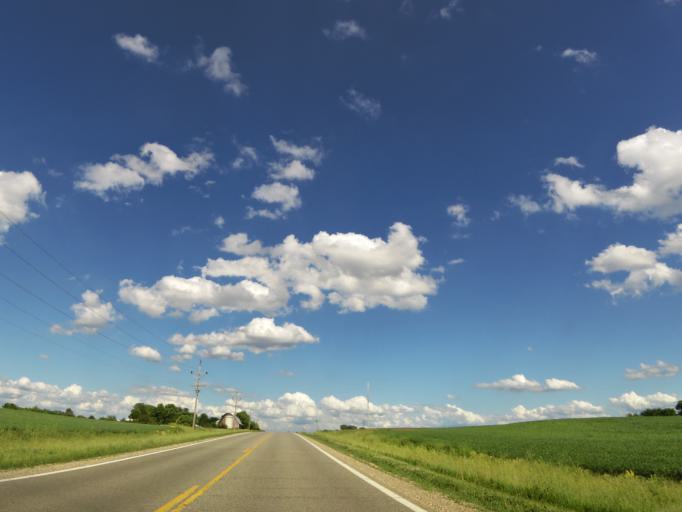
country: US
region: Minnesota
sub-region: Meeker County
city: Dassel
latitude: 45.0664
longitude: -94.2731
